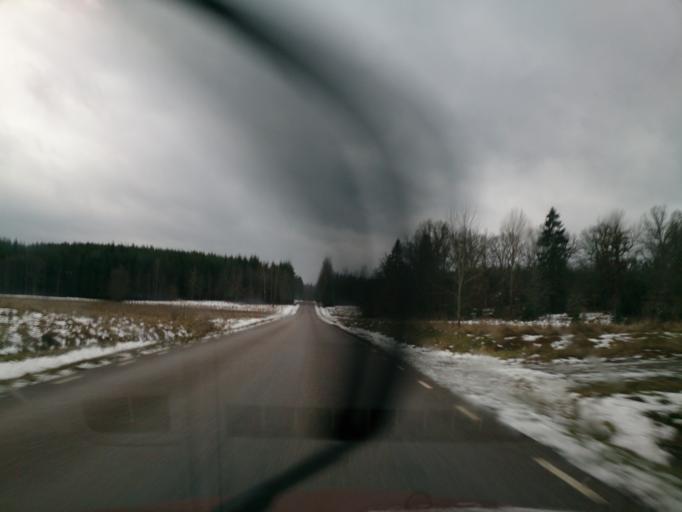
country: SE
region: OEstergoetland
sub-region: Atvidabergs Kommun
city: Atvidaberg
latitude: 58.2623
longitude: 16.0268
